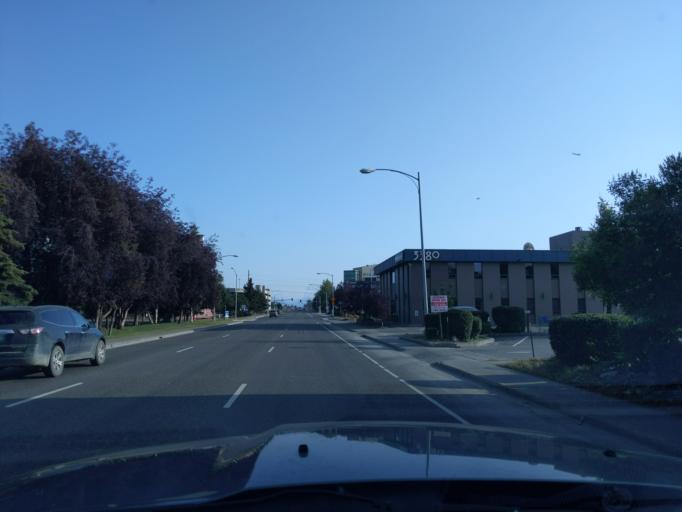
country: US
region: Alaska
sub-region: Anchorage Municipality
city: Anchorage
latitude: 61.1904
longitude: -149.8867
